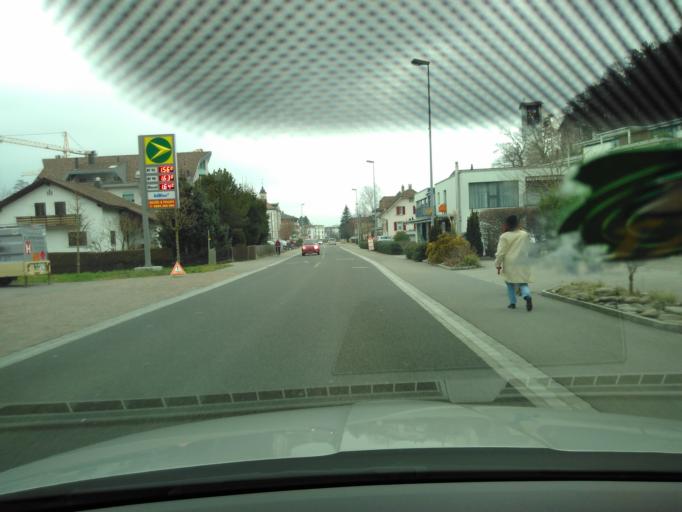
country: CH
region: Aargau
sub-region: Bezirk Aarau
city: Muhen
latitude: 47.3339
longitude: 8.0552
